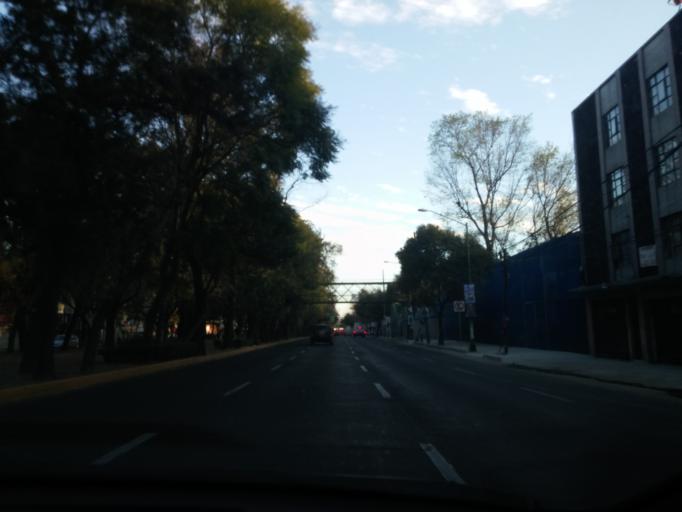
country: MX
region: Mexico City
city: Azcapotzalco
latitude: 19.4645
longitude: -99.1728
